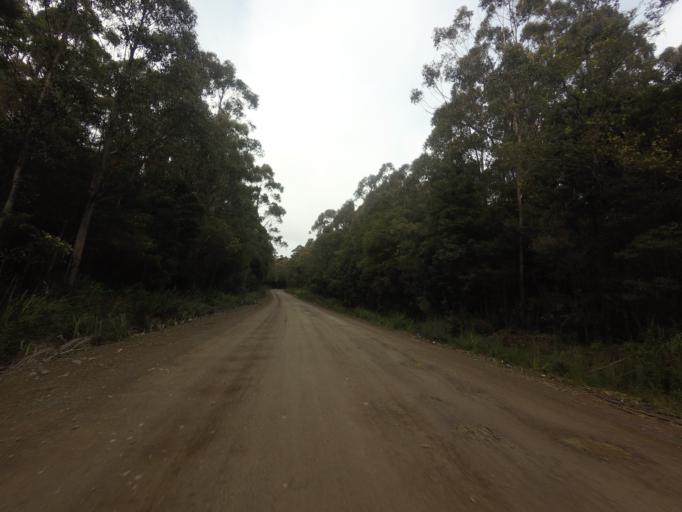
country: AU
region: Tasmania
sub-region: Huon Valley
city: Geeveston
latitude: -43.5135
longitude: 146.8854
